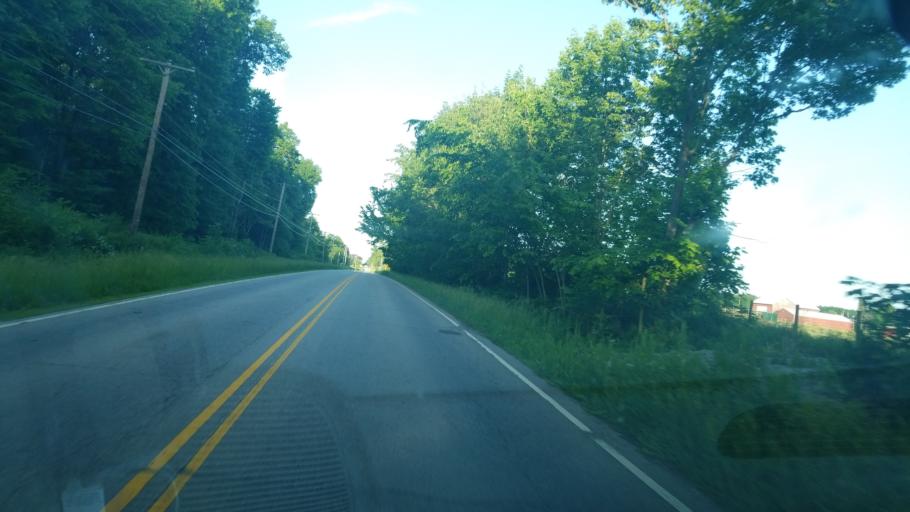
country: US
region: Ohio
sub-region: Mahoning County
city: Craig Beach
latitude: 41.0993
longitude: -80.9298
